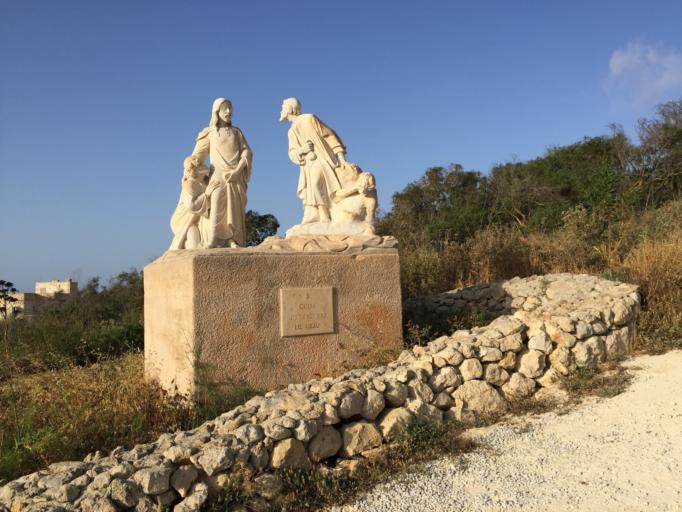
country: MT
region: L-Gharb
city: Gharb
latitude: 36.0611
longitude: 14.2171
